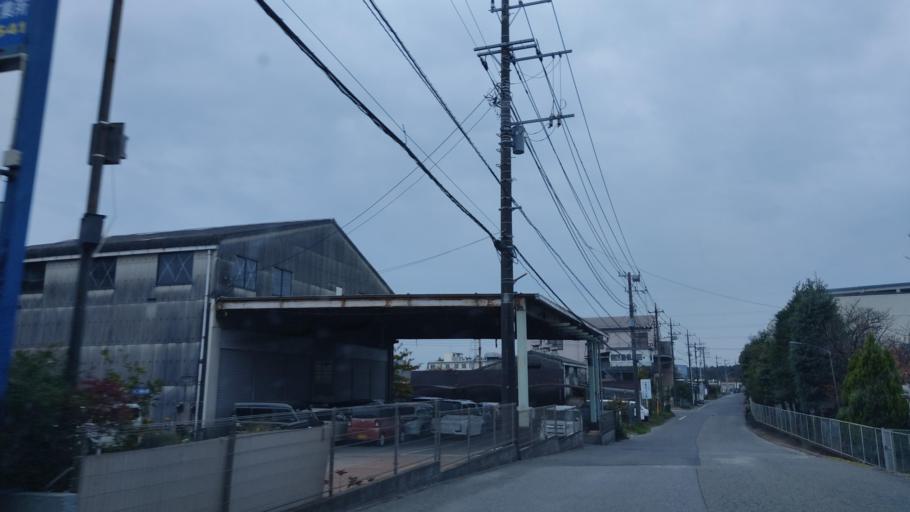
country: JP
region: Ibaraki
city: Moriya
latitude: 35.9082
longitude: 139.9533
